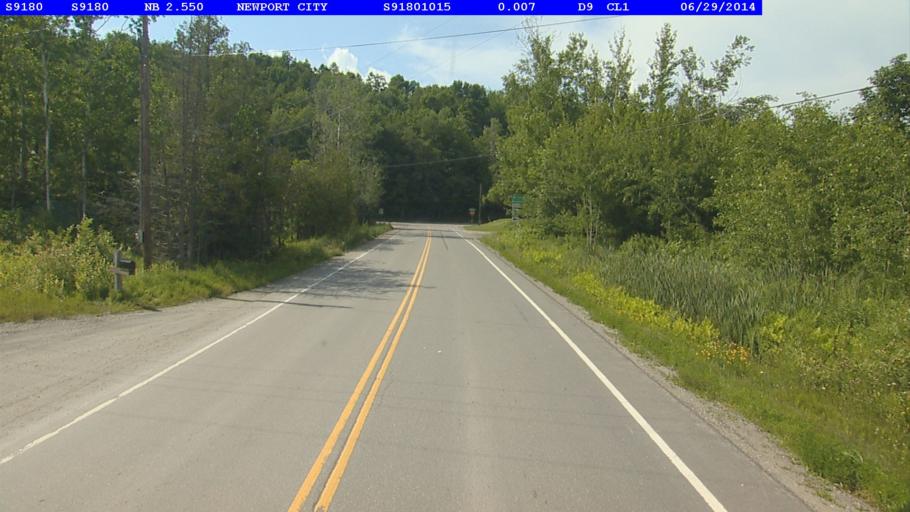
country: US
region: Vermont
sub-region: Orleans County
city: Newport
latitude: 44.9227
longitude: -72.2285
